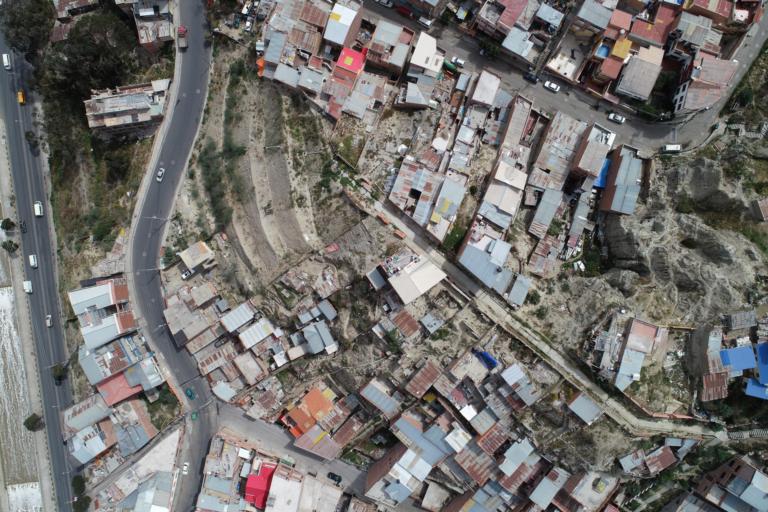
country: BO
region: La Paz
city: La Paz
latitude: -16.5376
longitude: -68.0941
